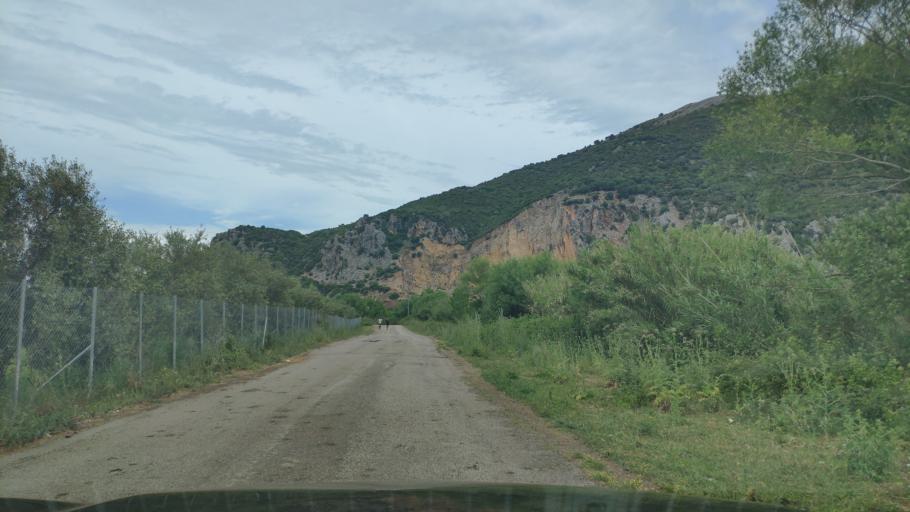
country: GR
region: West Greece
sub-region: Nomos Aitolias kai Akarnanias
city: Vonitsa
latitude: 38.9113
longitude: 20.9075
